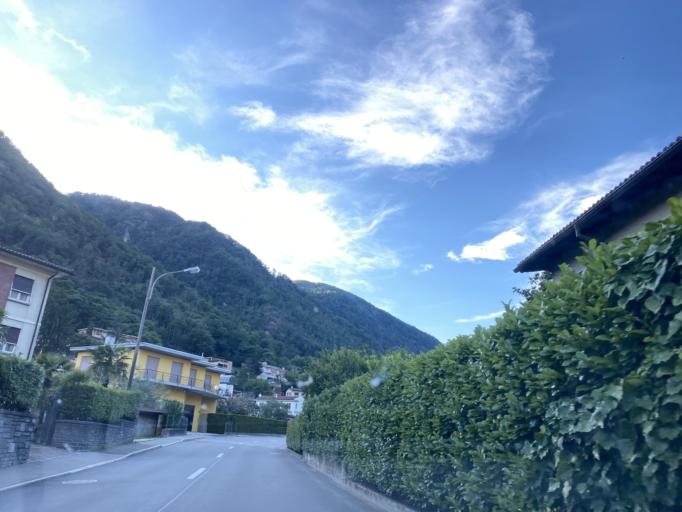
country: CH
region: Ticino
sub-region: Mendrisio District
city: Riva San Vitale
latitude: 45.9069
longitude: 8.9711
